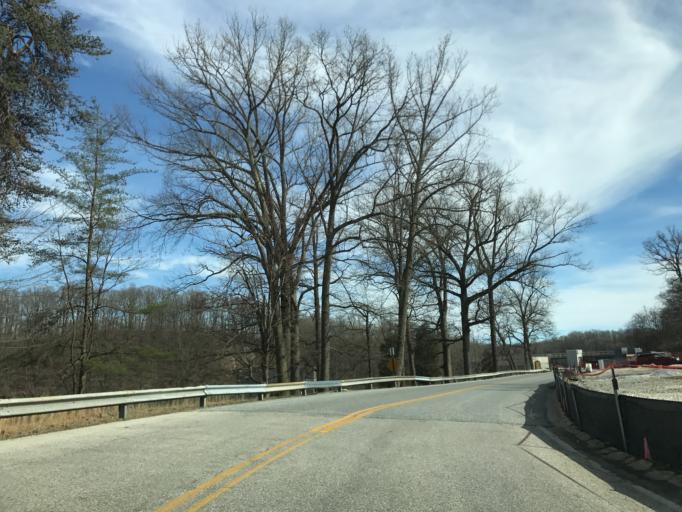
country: US
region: Maryland
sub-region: Baltimore County
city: Hampton
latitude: 39.4324
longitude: -76.5454
